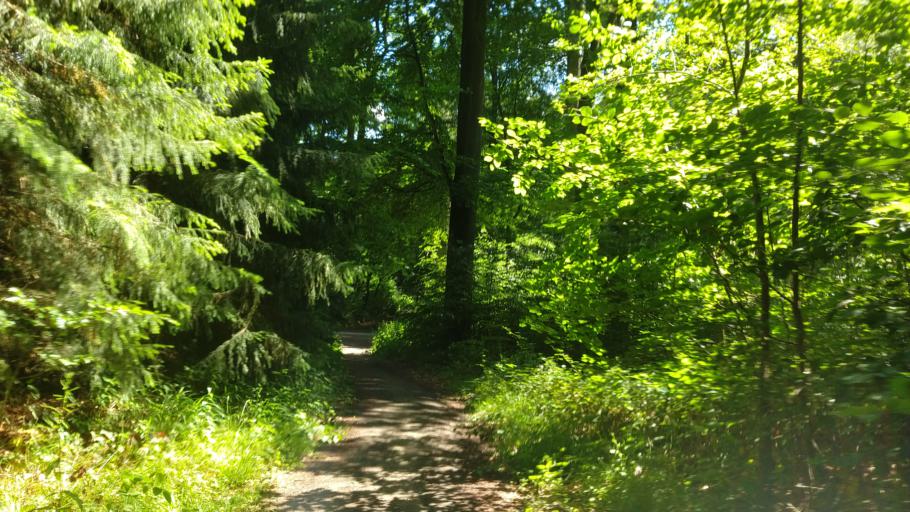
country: BE
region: Flanders
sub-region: Provincie Vlaams-Brabant
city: Bierbeek
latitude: 50.8104
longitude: 4.7342
